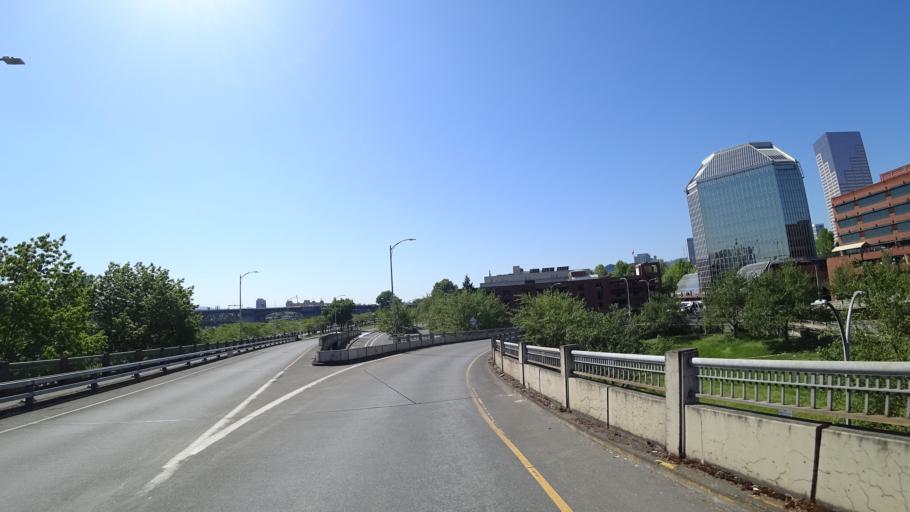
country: US
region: Oregon
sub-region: Multnomah County
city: Portland
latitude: 45.5262
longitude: -122.6708
